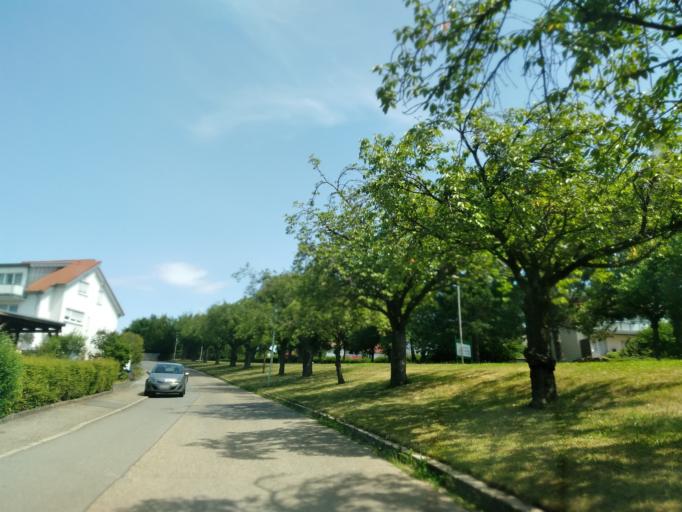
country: DE
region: Baden-Wuerttemberg
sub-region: Karlsruhe Region
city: Buchen
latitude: 49.5271
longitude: 9.3305
